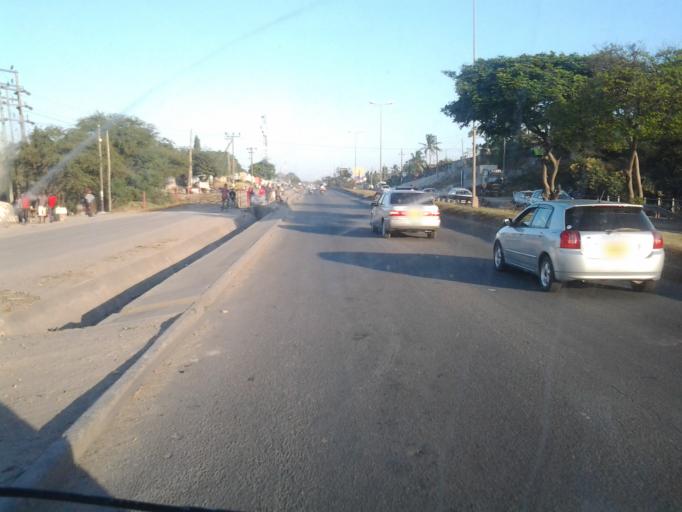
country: TZ
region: Dar es Salaam
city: Magomeni
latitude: -6.8208
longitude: 39.2281
